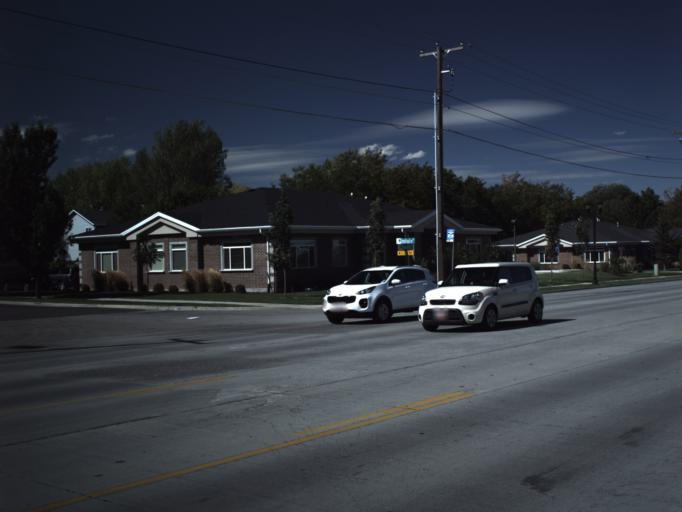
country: US
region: Utah
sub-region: Salt Lake County
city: South Jordan
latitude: 40.5695
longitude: -111.9386
